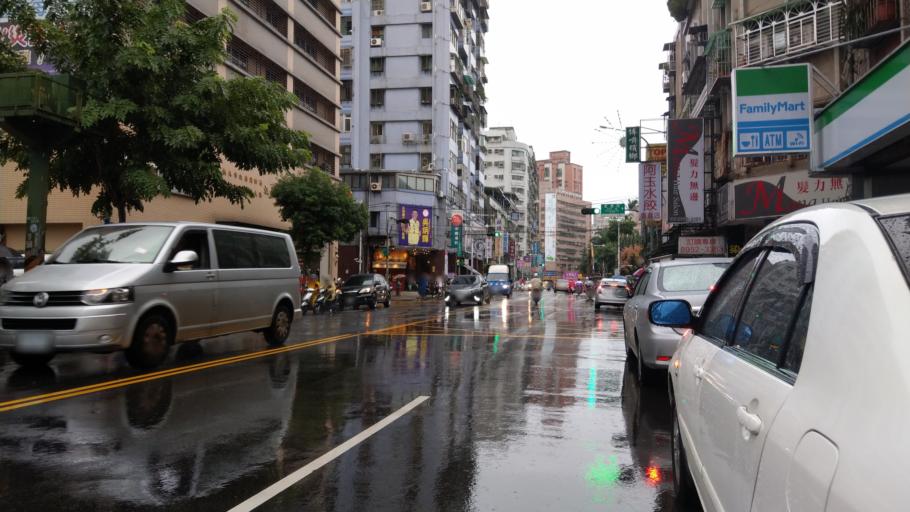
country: TW
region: Taipei
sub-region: Taipei
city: Banqiao
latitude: 24.9995
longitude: 121.4631
